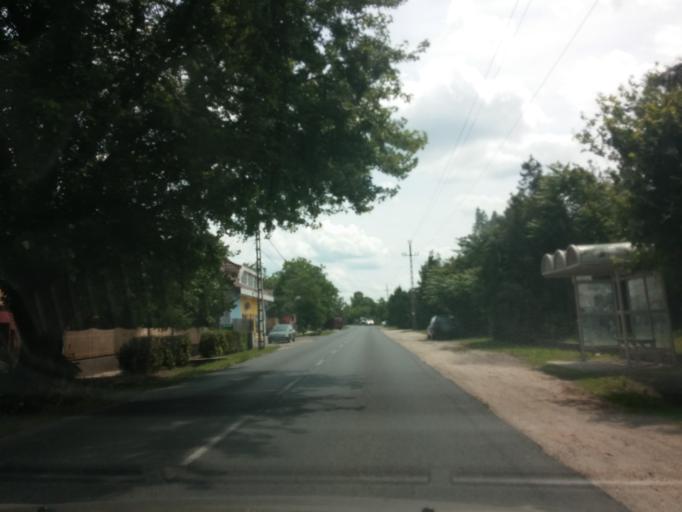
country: HU
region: Pest
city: Toekoel
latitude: 47.3157
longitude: 18.9642
